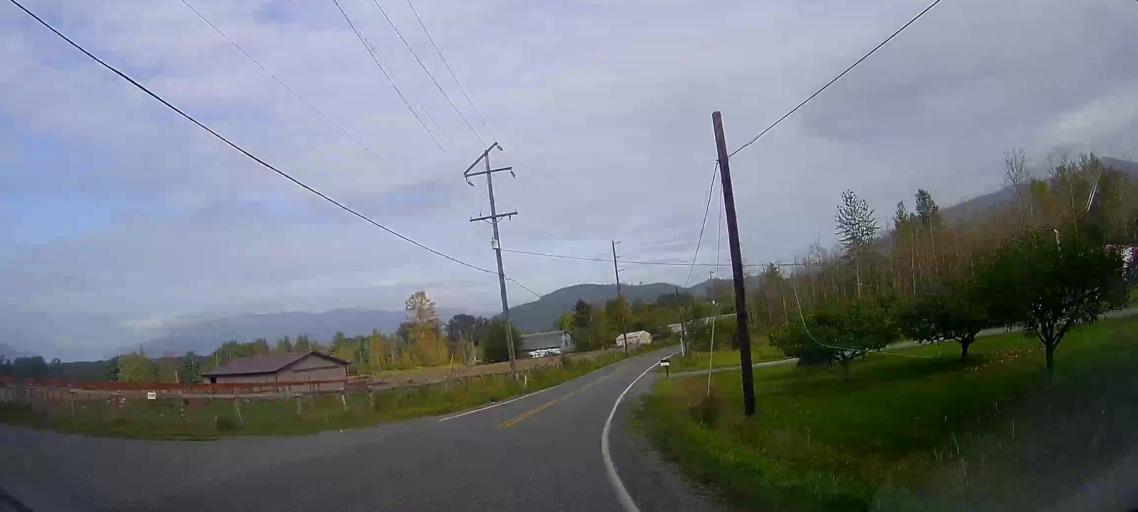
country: US
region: Washington
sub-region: Skagit County
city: Burlington
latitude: 48.4554
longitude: -122.2831
